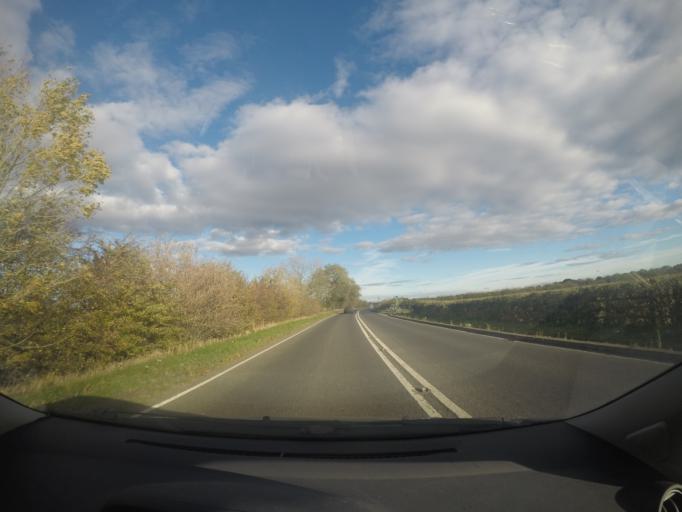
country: GB
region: England
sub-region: City and Borough of Leeds
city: Thorner
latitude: 53.8528
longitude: -1.3860
